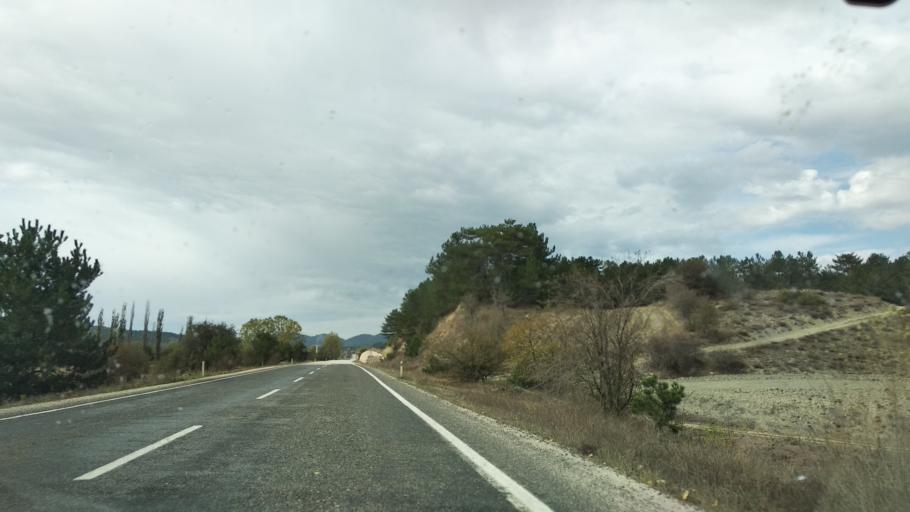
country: TR
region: Bolu
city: Mudurnu
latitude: 40.3951
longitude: 31.2055
